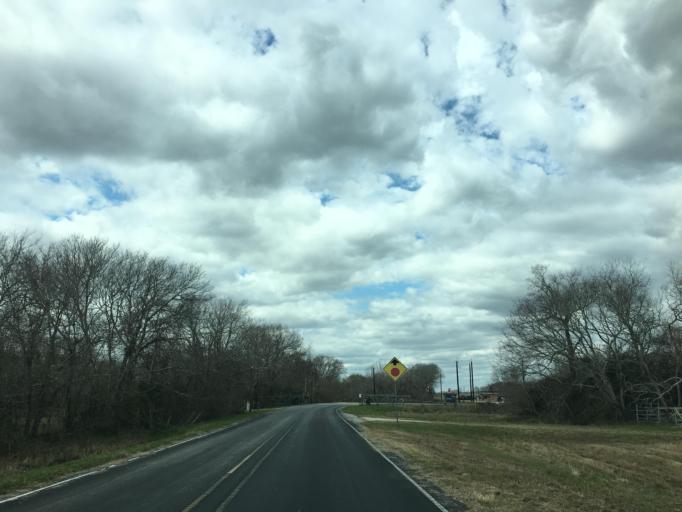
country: US
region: Texas
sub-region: Brazoria County
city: Oyster Creek
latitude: 29.0651
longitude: -95.3179
